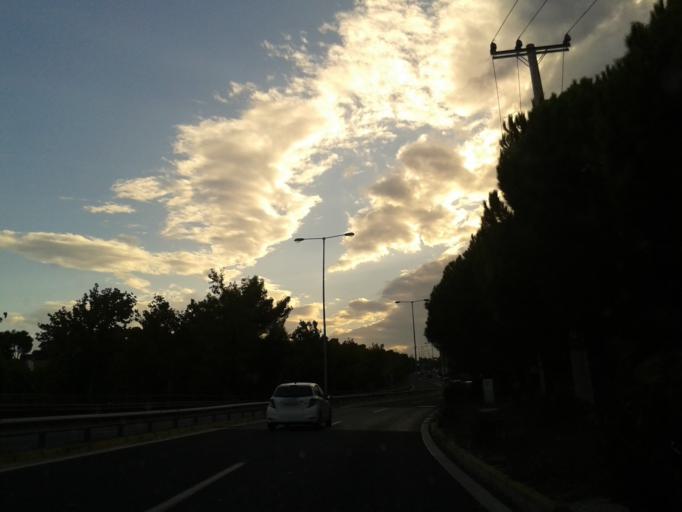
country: GR
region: Attica
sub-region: Nomarchia Anatolikis Attikis
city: Neos Voutzas
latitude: 38.0365
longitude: 23.9889
